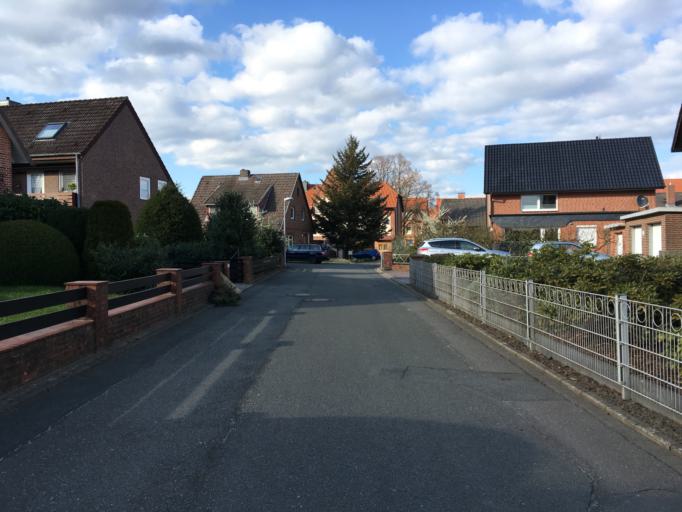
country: DE
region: Lower Saxony
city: Lueneburg
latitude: 53.2447
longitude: 10.4406
